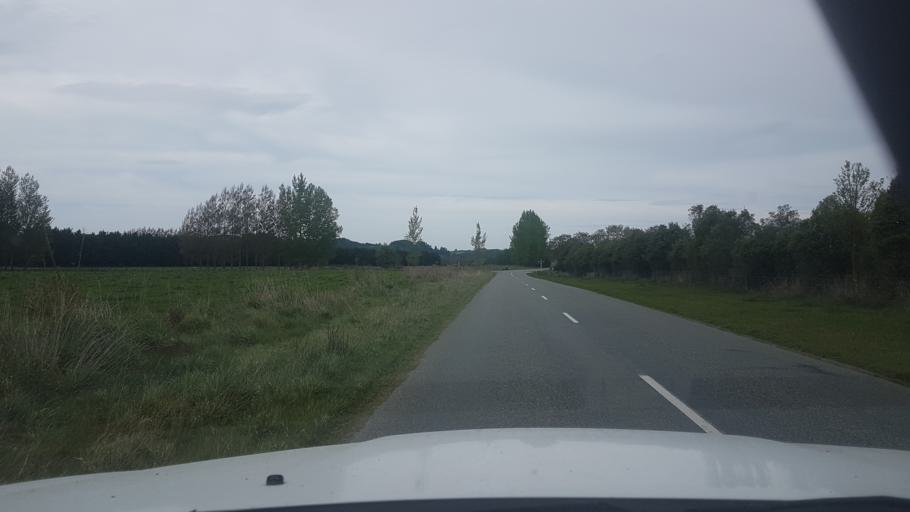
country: NZ
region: Canterbury
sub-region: Timaru District
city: Pleasant Point
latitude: -44.0741
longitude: 171.1688
